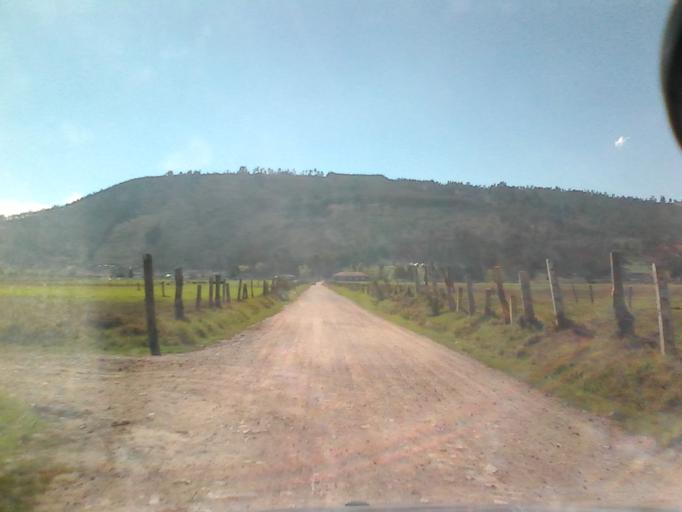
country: CO
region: Boyaca
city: Duitama
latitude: 5.7859
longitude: -73.0291
